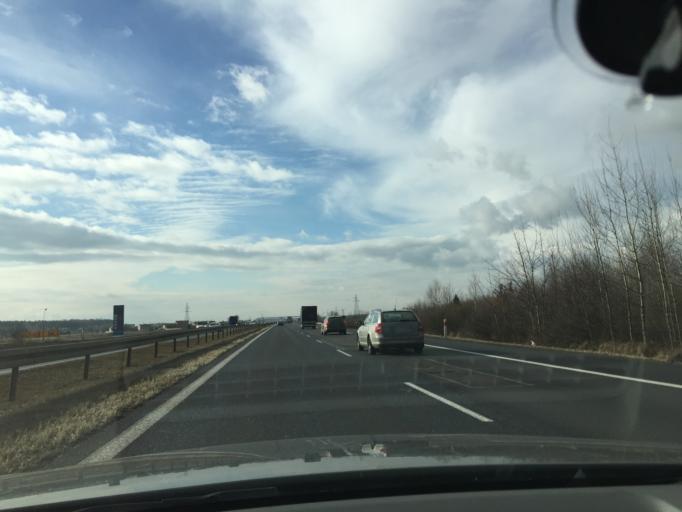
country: PL
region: Lodz Voivodeship
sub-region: Powiat piotrkowski
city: Wola Krzysztoporska
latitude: 51.3457
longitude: 19.6000
